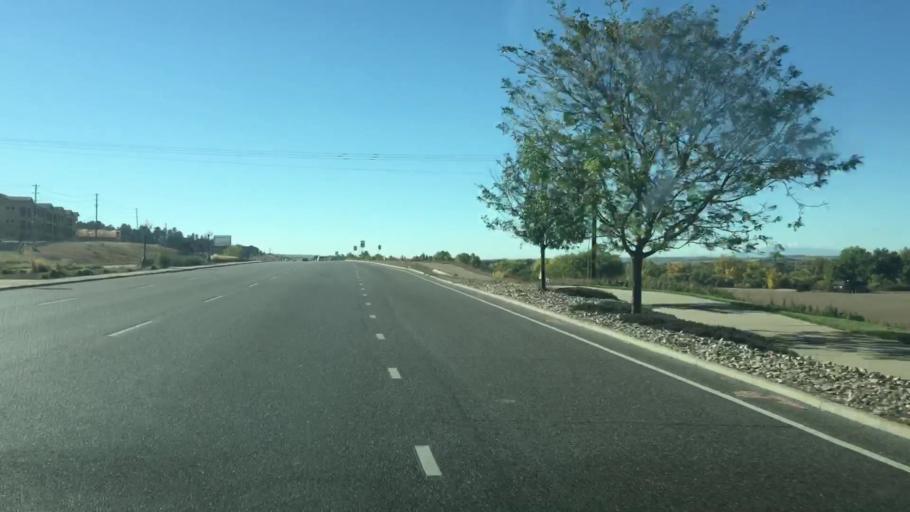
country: US
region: Colorado
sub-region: Douglas County
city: Parker
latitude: 39.5082
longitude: -104.7636
